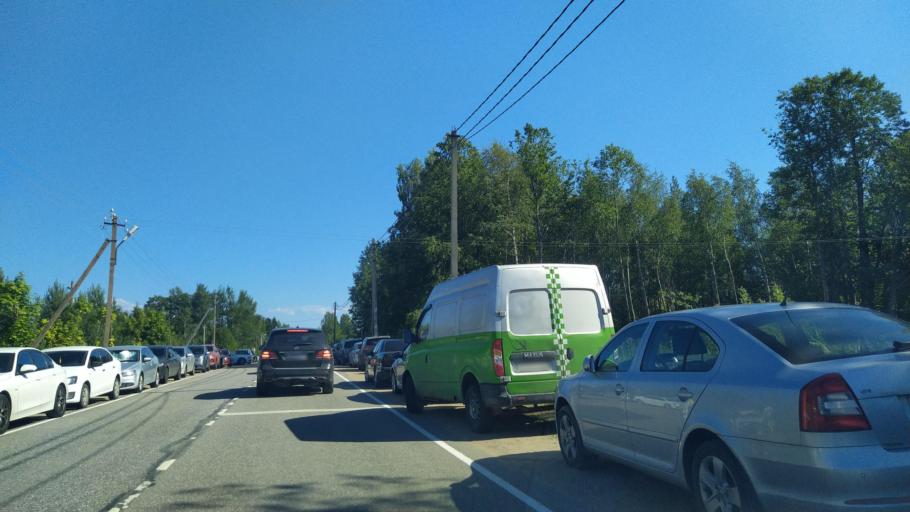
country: RU
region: Leningrad
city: Borisova Griva
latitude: 60.1183
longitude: 31.0777
